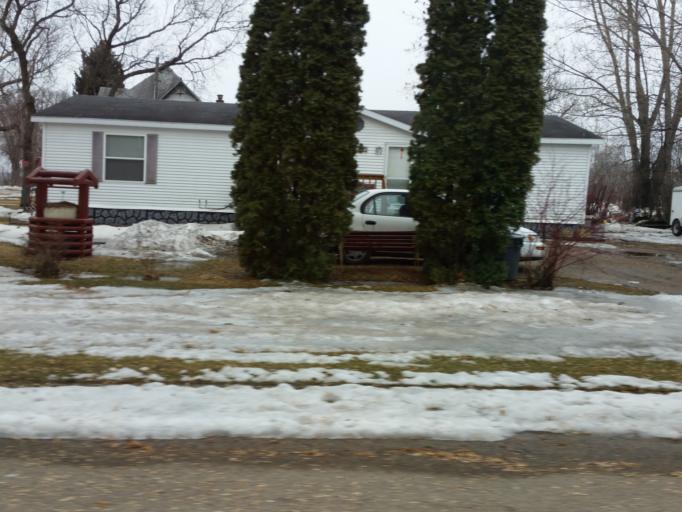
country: US
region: North Dakota
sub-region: Walsh County
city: Grafton
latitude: 48.6171
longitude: -97.4453
